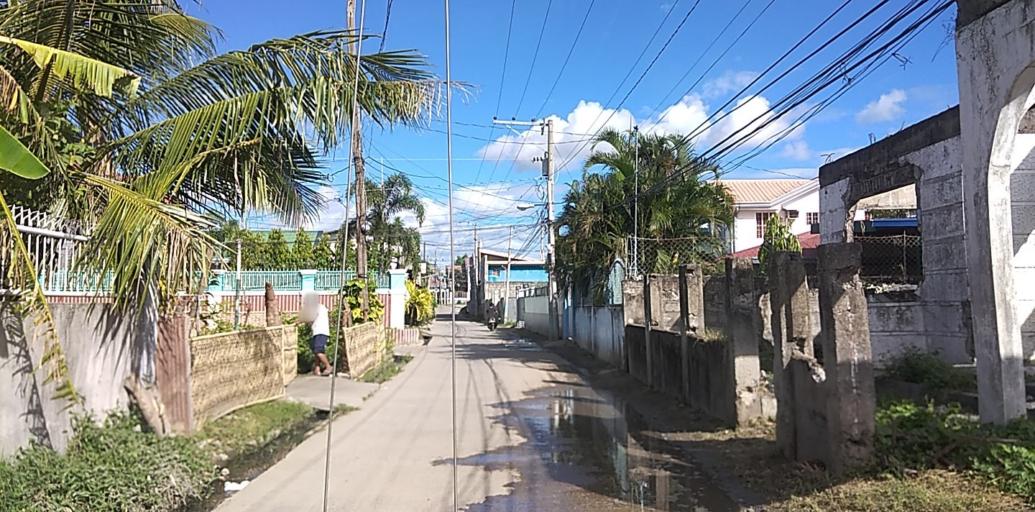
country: PH
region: Central Luzon
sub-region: Province of Pampanga
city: Arayat
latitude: 15.1390
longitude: 120.7719
